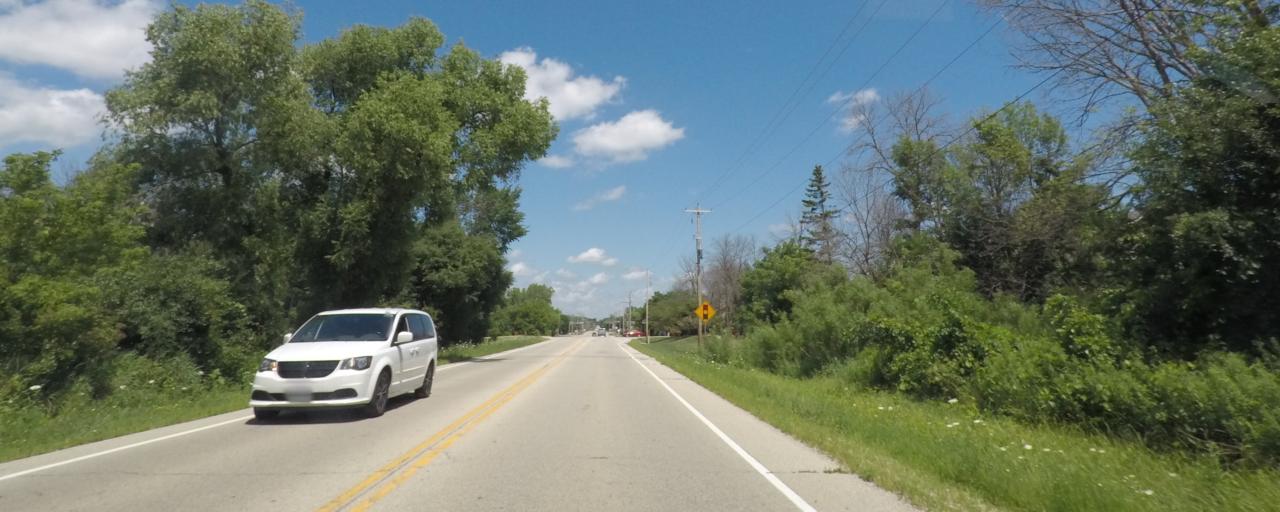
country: US
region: Wisconsin
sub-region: Waukesha County
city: Waukesha
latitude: 43.0463
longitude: -88.1858
